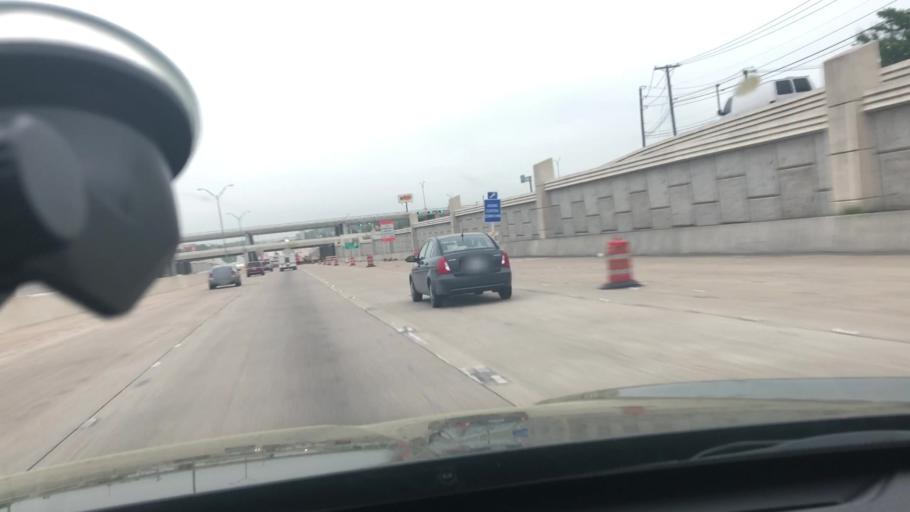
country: US
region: Texas
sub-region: Bell County
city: Temple
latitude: 31.0896
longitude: -97.3901
